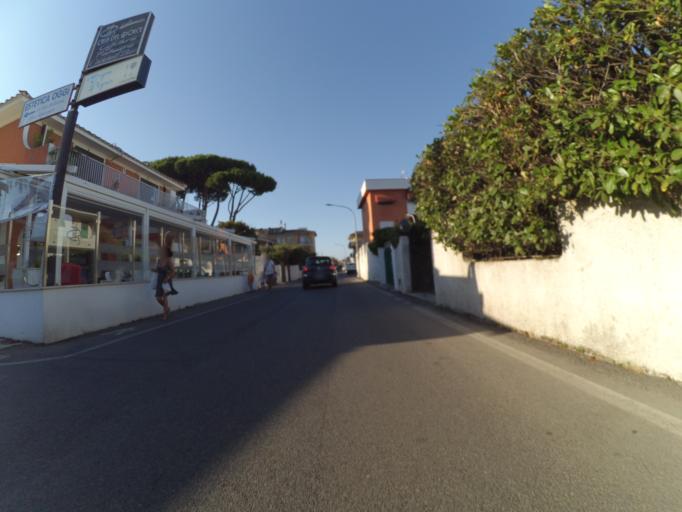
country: IT
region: Latium
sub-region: Provincia di Latina
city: San Felice Circeo
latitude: 41.2416
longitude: 13.0949
